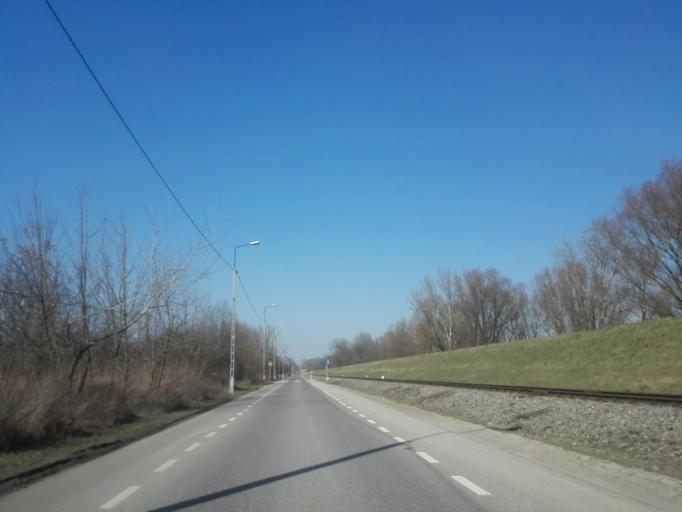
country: PL
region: Masovian Voivodeship
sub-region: Warszawa
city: Wilanow
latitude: 52.1779
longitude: 21.1155
